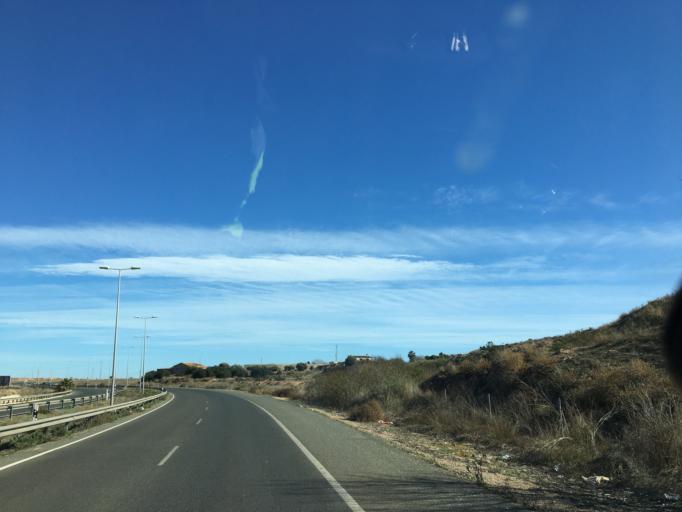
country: ES
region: Murcia
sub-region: Murcia
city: Cartagena
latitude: 37.6351
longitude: -0.9979
